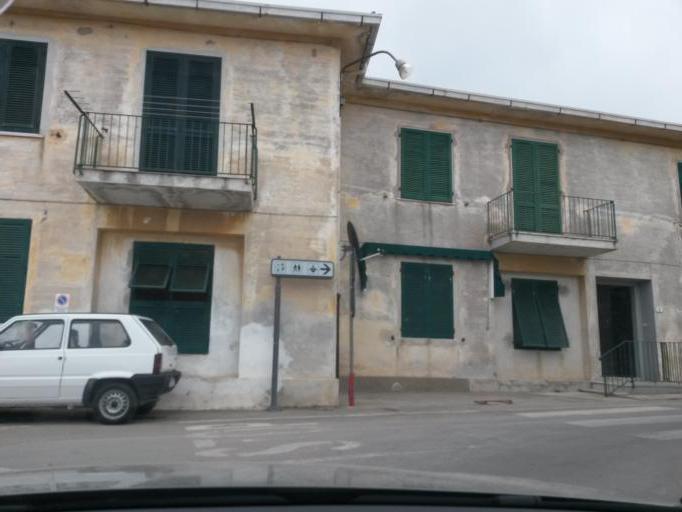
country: IT
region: Tuscany
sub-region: Provincia di Livorno
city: Capoliveri
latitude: 42.7428
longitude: 10.3807
